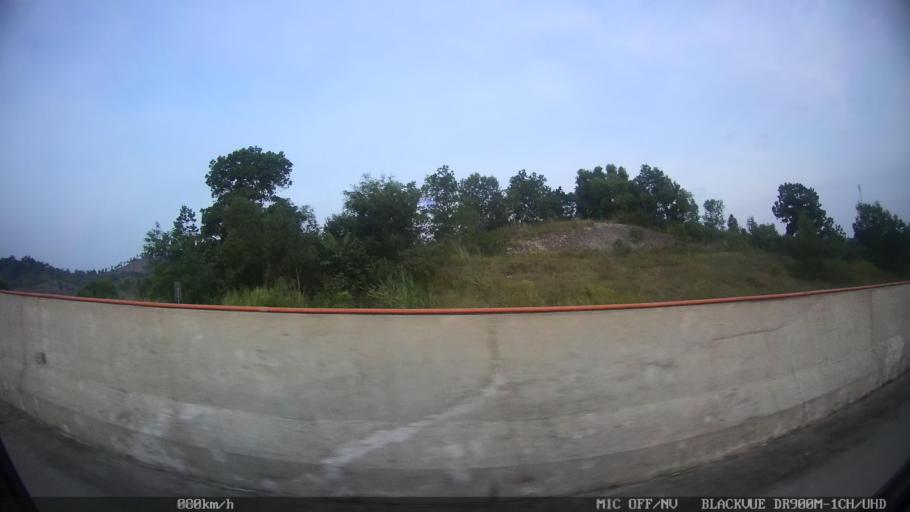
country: ID
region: Lampung
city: Penengahan
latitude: -5.8357
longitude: 105.7310
